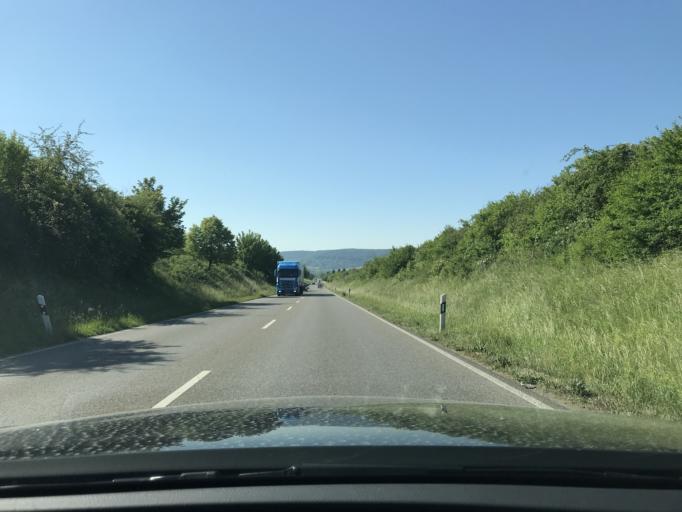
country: DE
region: Baden-Wuerttemberg
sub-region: Regierungsbezirk Stuttgart
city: Fellbach
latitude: 48.8323
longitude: 9.2891
